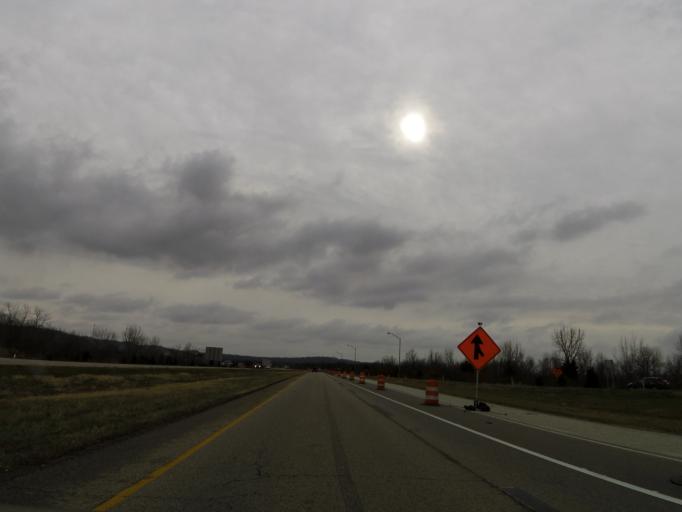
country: US
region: Indiana
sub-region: Dearborn County
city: Greendale
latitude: 39.1203
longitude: -84.8337
